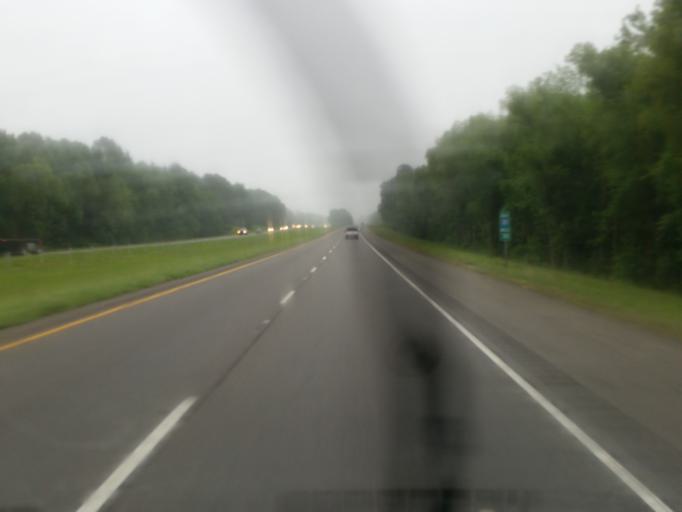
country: US
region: Louisiana
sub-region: Bossier Parish
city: Eastwood
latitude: 32.5419
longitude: -93.5777
